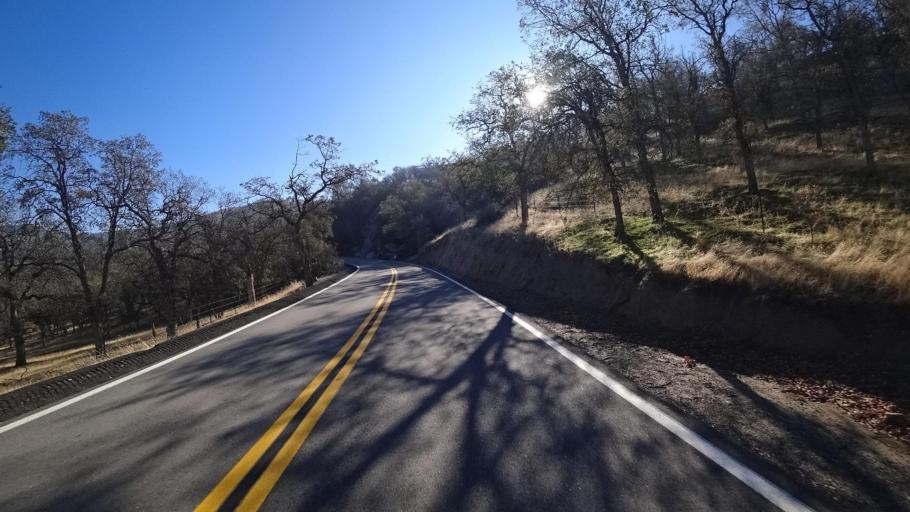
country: US
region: California
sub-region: Kern County
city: Alta Sierra
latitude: 35.7200
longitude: -118.7963
